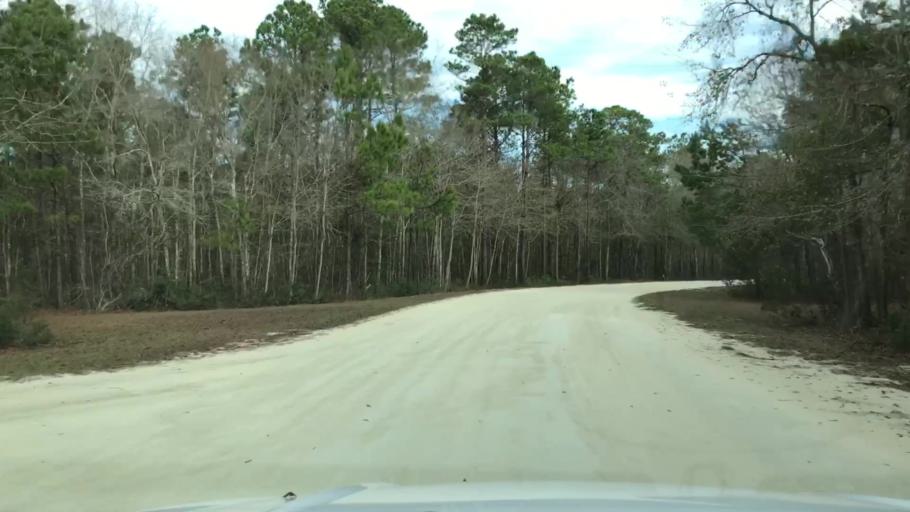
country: US
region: South Carolina
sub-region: Charleston County
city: Isle of Palms
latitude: 32.9013
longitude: -79.7261
